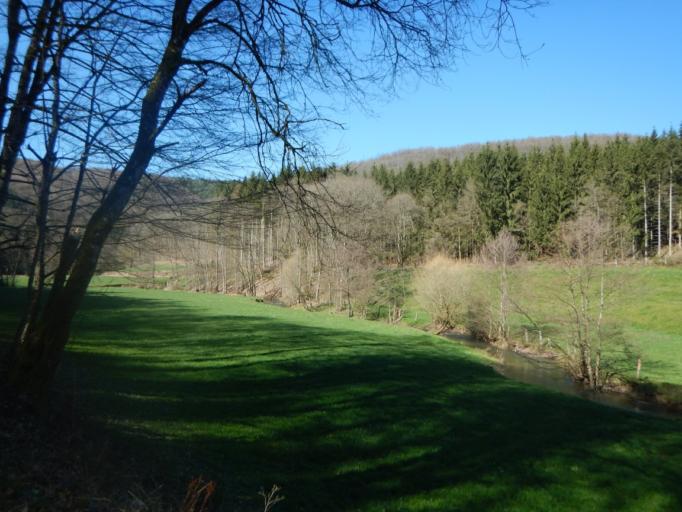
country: LU
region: Diekirch
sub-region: Canton de Wiltz
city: Wilwerwiltz
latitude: 49.9712
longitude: 5.9726
